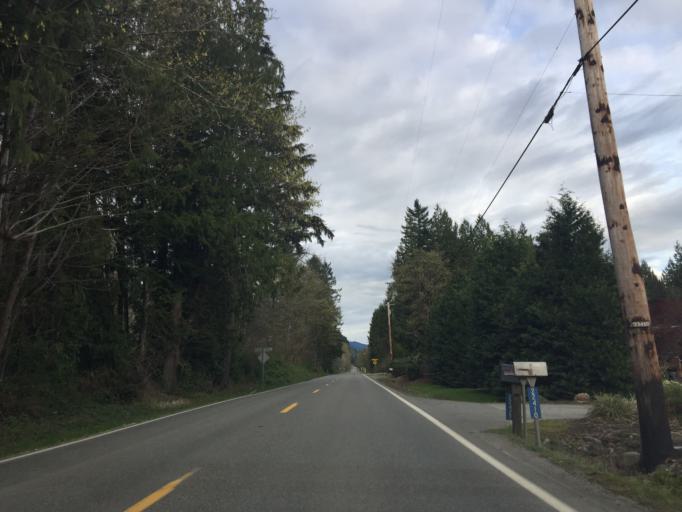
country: US
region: Washington
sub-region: Snohomish County
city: Arlington Heights
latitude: 48.2715
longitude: -121.9271
